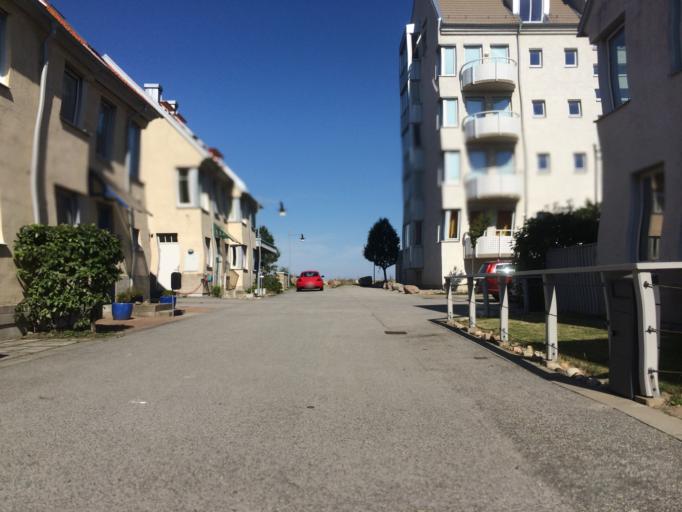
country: SE
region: Skane
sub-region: Malmo
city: Bunkeflostrand
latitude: 55.5890
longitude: 12.9193
